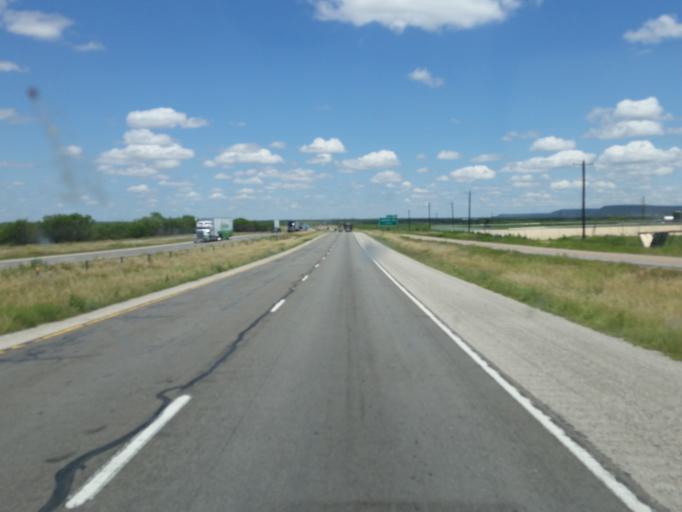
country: US
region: Texas
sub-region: Nolan County
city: Sweetwater
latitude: 32.4936
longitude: -100.2579
